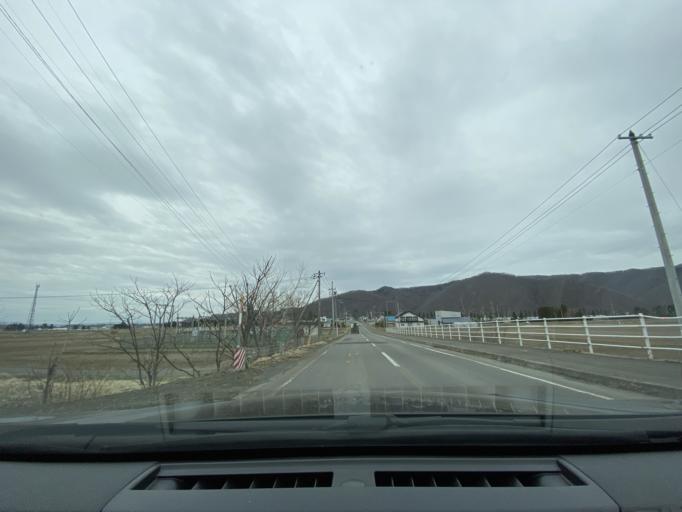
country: JP
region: Hokkaido
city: Nayoro
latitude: 44.1291
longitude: 142.4848
